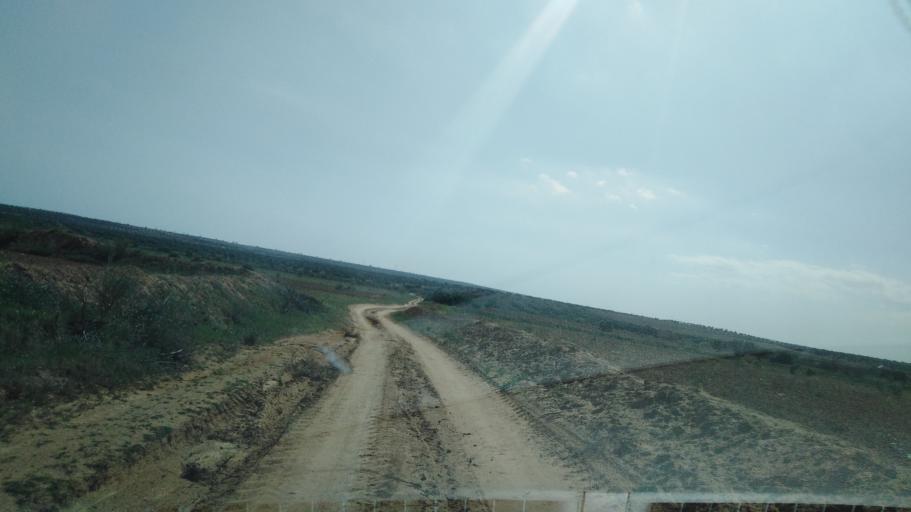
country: TN
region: Safaqis
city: Bi'r `Ali Bin Khalifah
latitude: 34.7832
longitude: 10.3675
